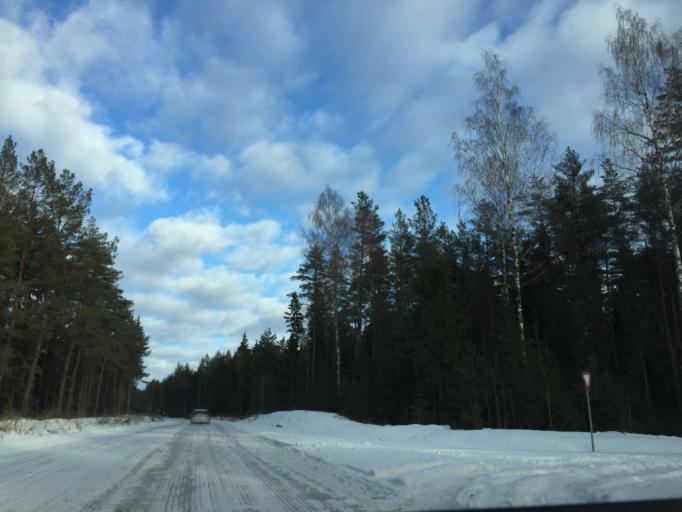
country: LV
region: Ogre
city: Jumprava
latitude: 56.5703
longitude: 24.9342
